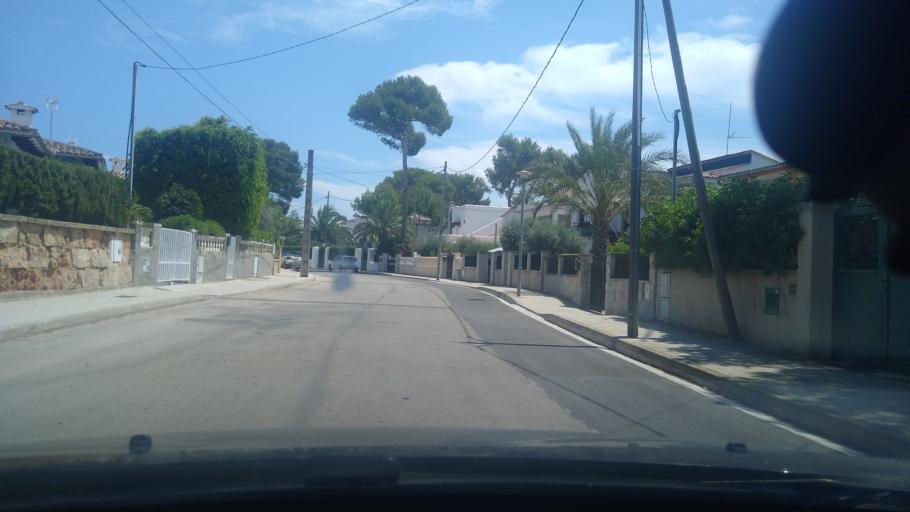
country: ES
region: Balearic Islands
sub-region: Illes Balears
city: Santa Margalida
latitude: 39.7587
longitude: 3.1613
